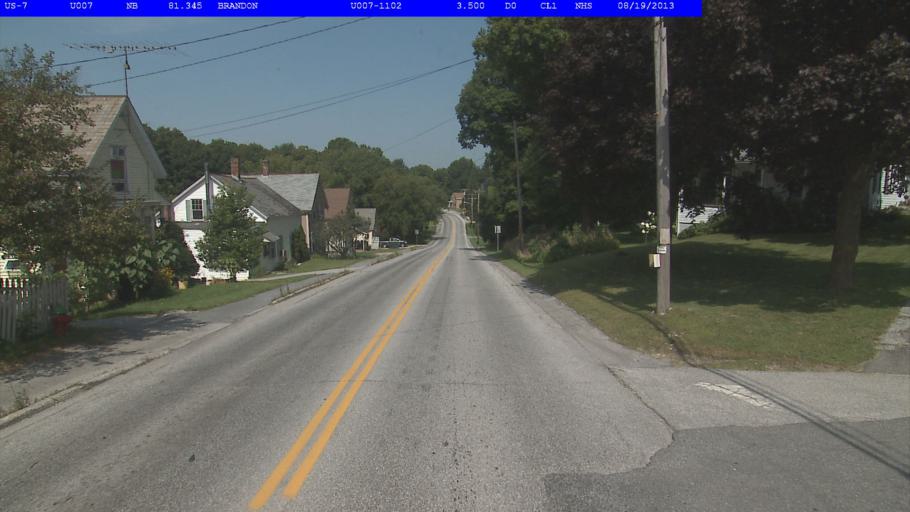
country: US
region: Vermont
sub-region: Rutland County
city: Brandon
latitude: 43.7949
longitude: -73.0805
